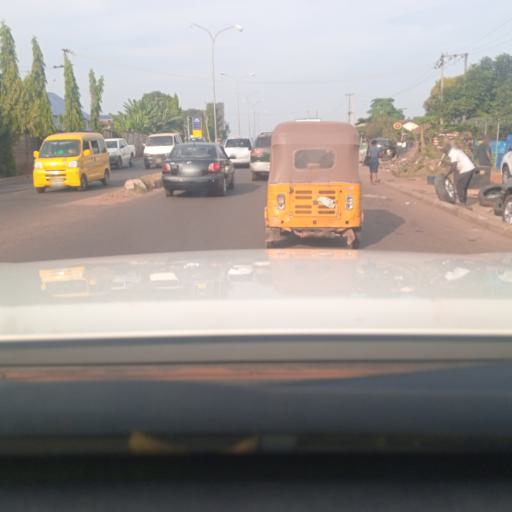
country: NG
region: Enugu
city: Enugu
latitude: 6.4495
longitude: 7.5014
